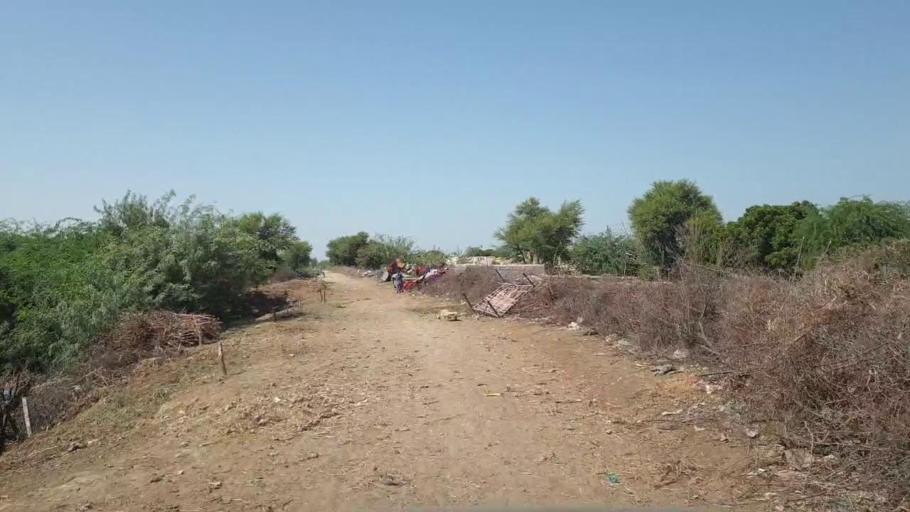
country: PK
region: Sindh
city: Matiari
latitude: 25.6323
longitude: 68.4899
